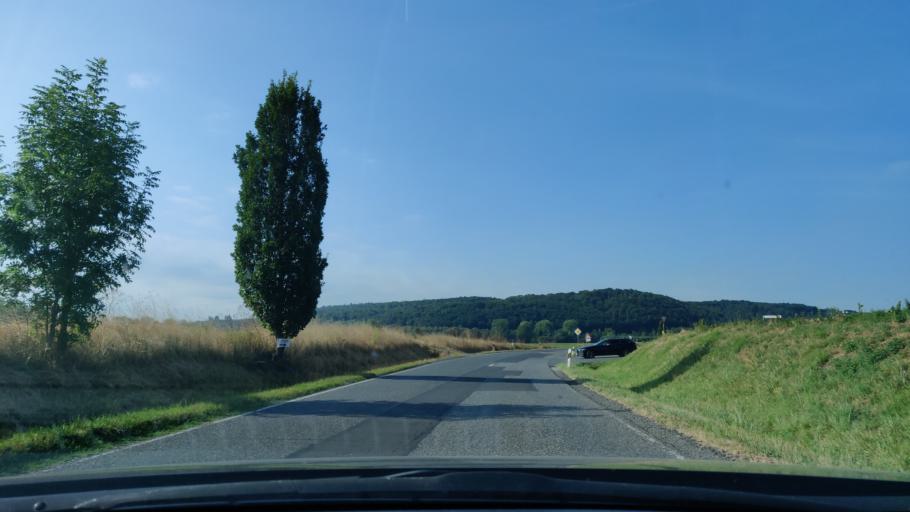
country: DE
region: Hesse
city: Fritzlar
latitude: 51.1339
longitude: 9.2486
